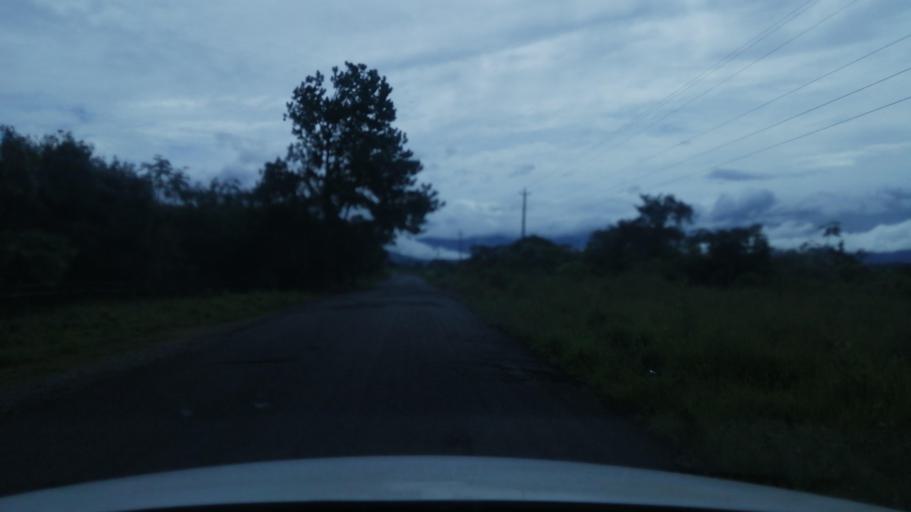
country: PA
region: Chiriqui
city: Potrerillos Abajo
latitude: 8.6704
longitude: -82.4405
